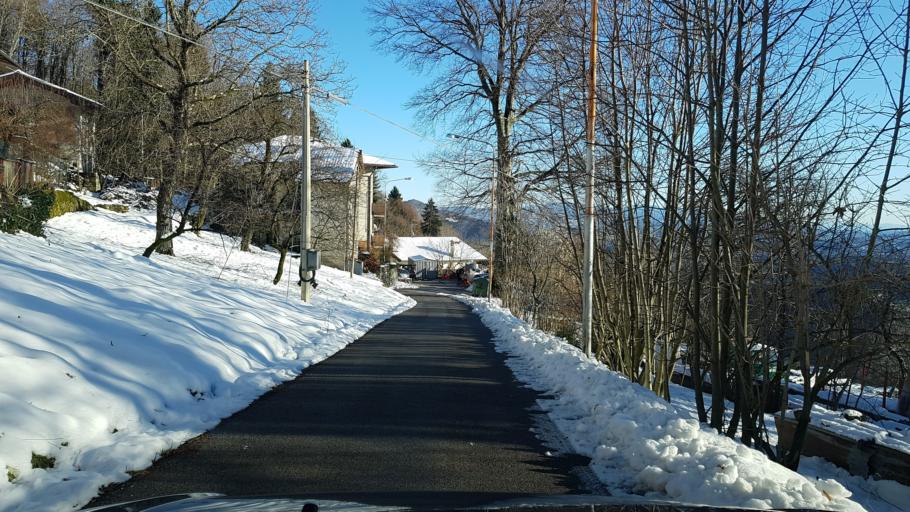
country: IT
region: Friuli Venezia Giulia
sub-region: Provincia di Udine
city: Savogna
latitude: 46.1941
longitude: 13.5306
